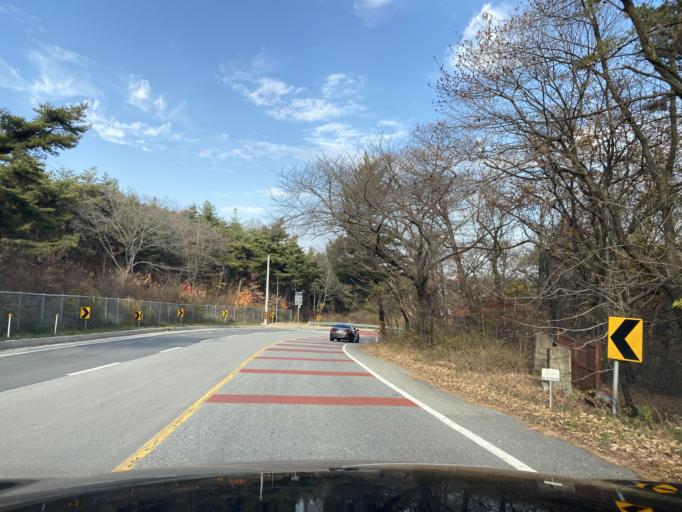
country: KR
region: Chungcheongnam-do
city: Hongsung
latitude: 36.6652
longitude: 126.6355
